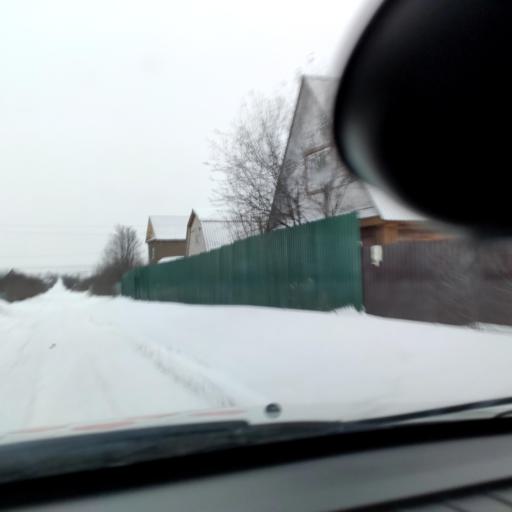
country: RU
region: Bashkortostan
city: Avdon
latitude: 54.5730
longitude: 55.7360
